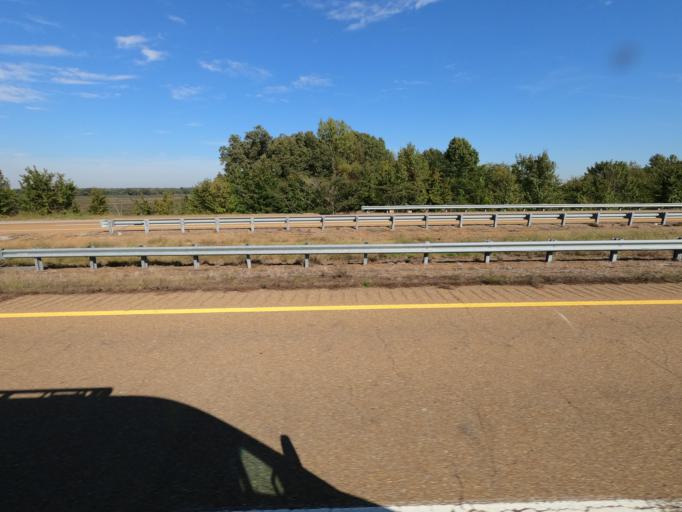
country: US
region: Tennessee
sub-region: Shelby County
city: Lakeland
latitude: 35.3099
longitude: -89.7784
